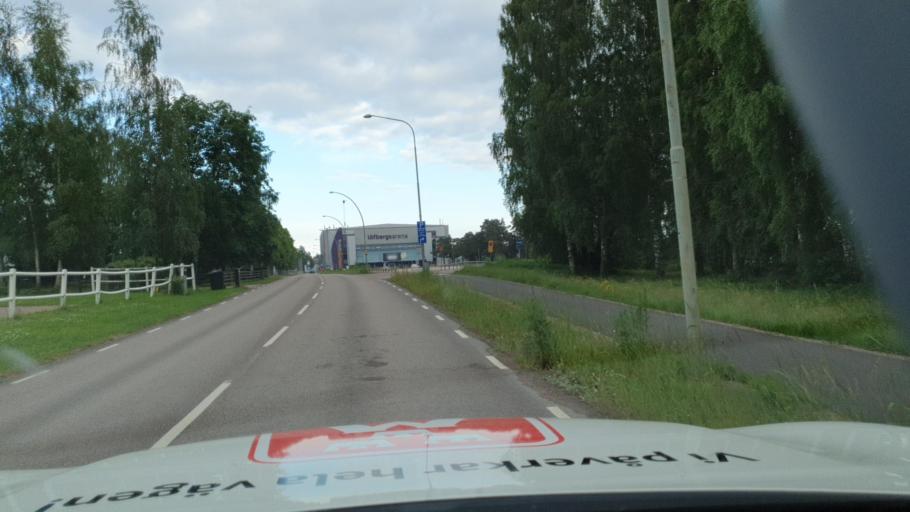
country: SE
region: Vaermland
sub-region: Karlstads Kommun
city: Karlstad
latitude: 59.4108
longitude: 13.4961
